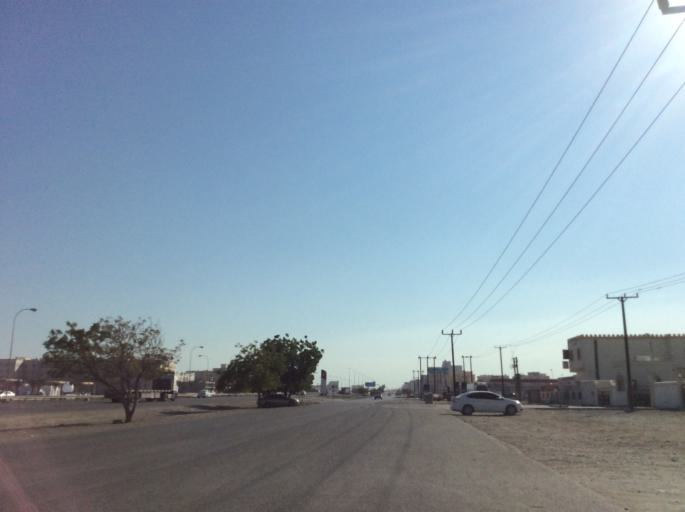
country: OM
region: Al Batinah
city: Al Liwa'
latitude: 24.4450
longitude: 56.6078
